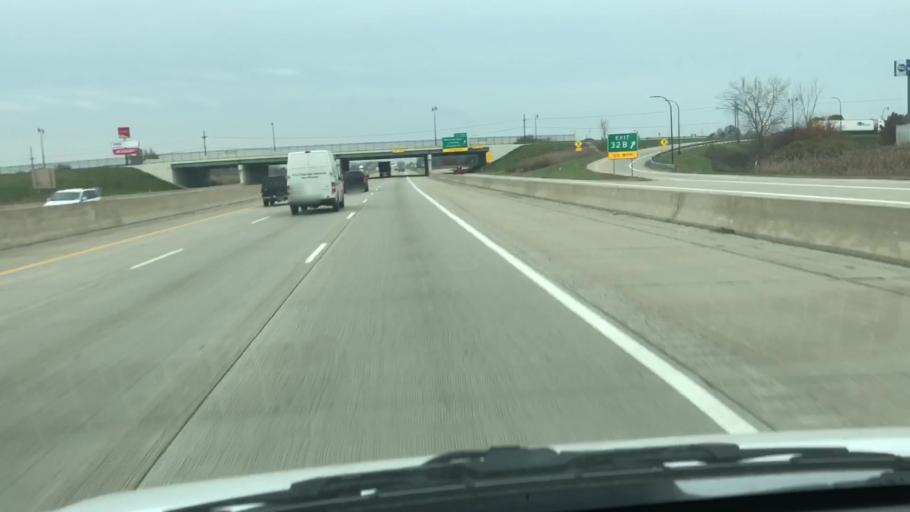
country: US
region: Michigan
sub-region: Wayne County
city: Woodhaven
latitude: 42.1407
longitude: -83.2418
